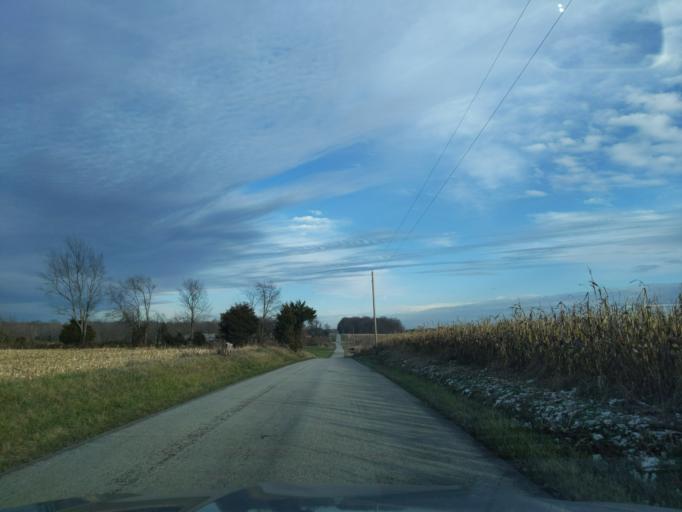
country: US
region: Indiana
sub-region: Decatur County
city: Westport
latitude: 39.2192
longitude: -85.4848
